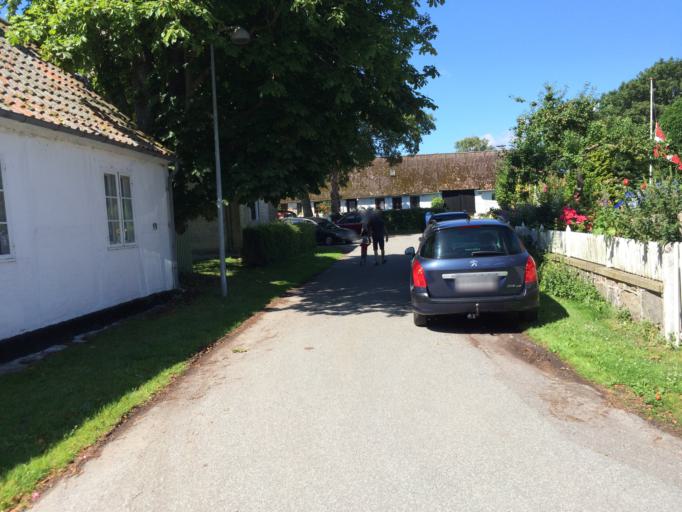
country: DK
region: Zealand
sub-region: Vordingborg Kommune
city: Stege
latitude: 55.0416
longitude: 12.1950
